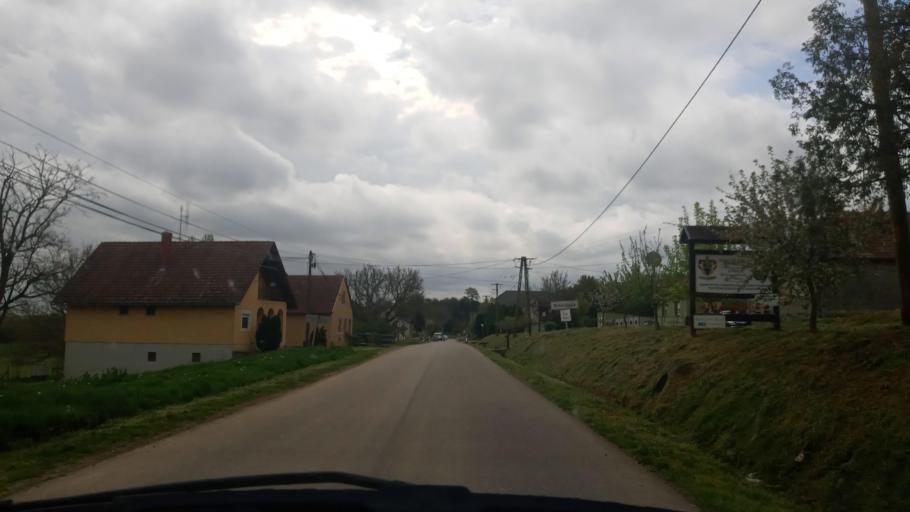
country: HU
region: Baranya
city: Boly
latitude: 45.9788
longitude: 18.4238
